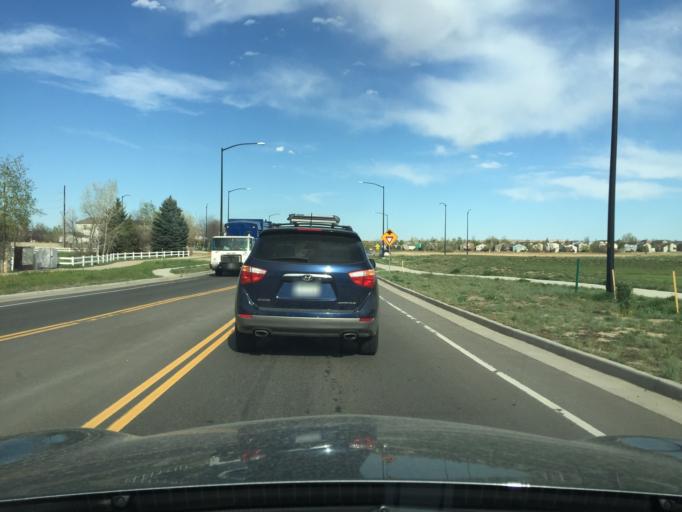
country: US
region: Colorado
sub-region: Boulder County
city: Erie
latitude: 40.0368
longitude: -105.0760
